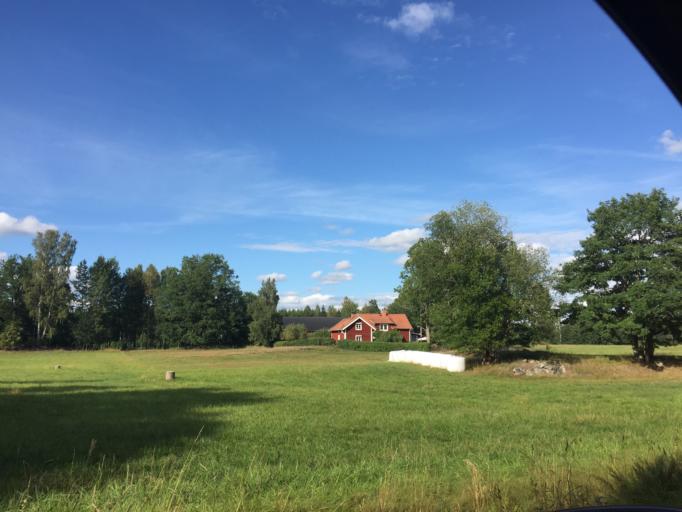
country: SE
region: OErebro
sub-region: Hallsbergs Kommun
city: Palsboda
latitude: 58.8847
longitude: 15.5504
